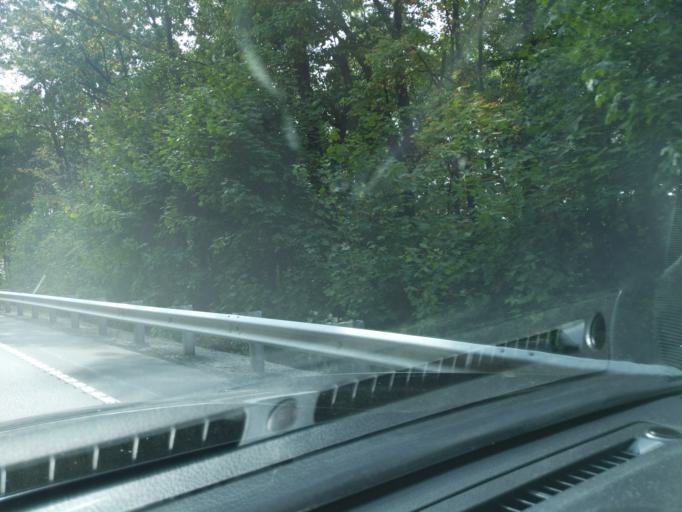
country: US
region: Pennsylvania
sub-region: Blair County
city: Lakemont
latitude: 40.4681
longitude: -78.3864
